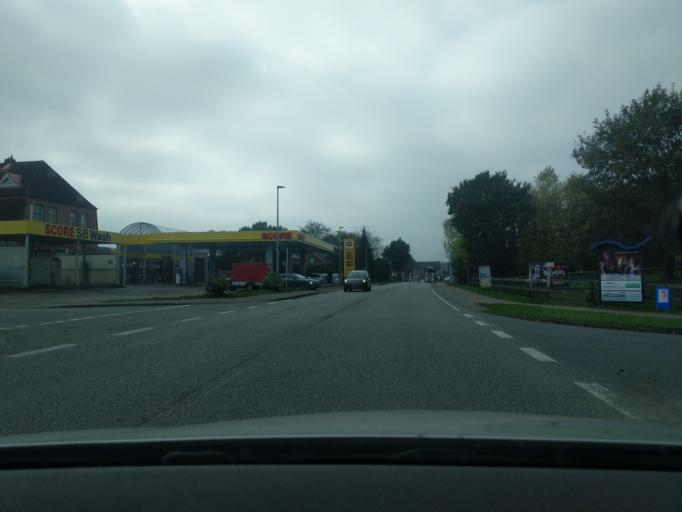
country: DE
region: Lower Saxony
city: Otterndorf
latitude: 53.8098
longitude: 8.9132
